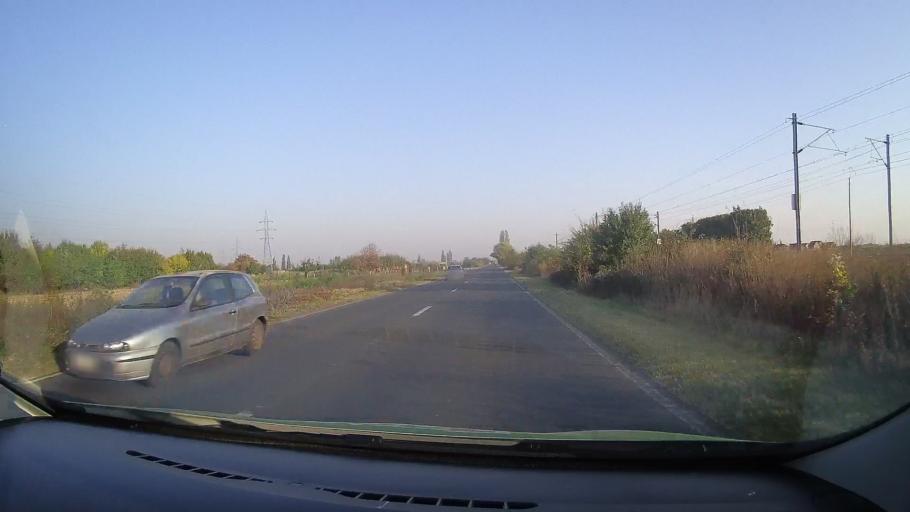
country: RO
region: Arad
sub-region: Comuna Curtici
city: Curtici
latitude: 46.3225
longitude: 21.3063
